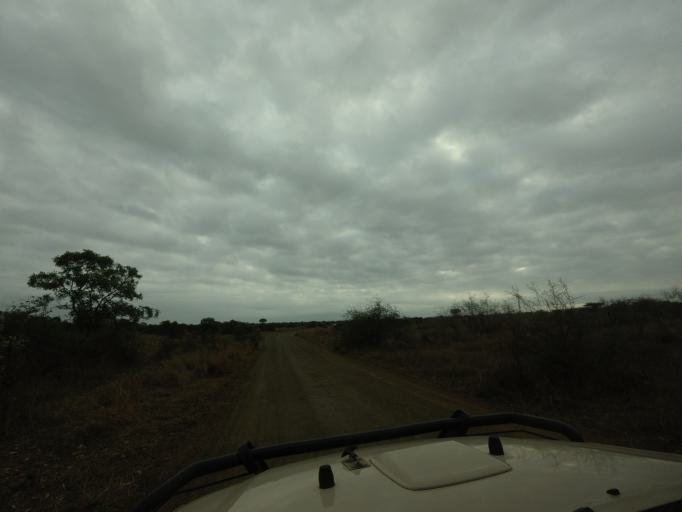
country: ZA
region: Mpumalanga
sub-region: Ehlanzeni District
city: Komatipoort
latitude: -25.3306
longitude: 31.9029
